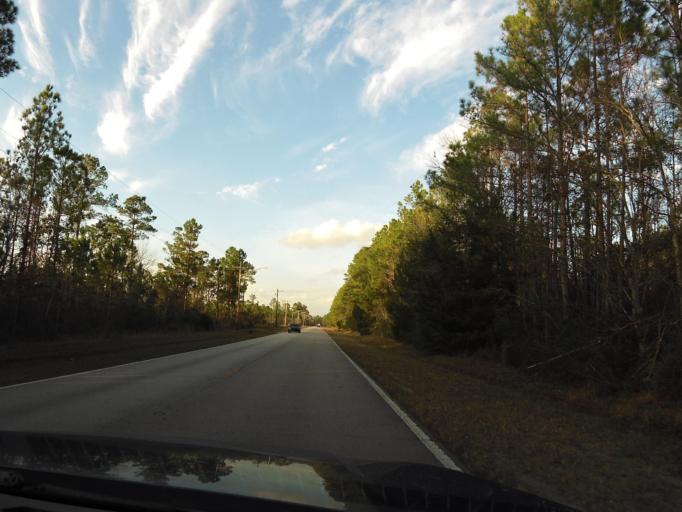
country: US
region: Florida
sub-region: Duval County
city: Baldwin
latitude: 30.1950
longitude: -81.9911
